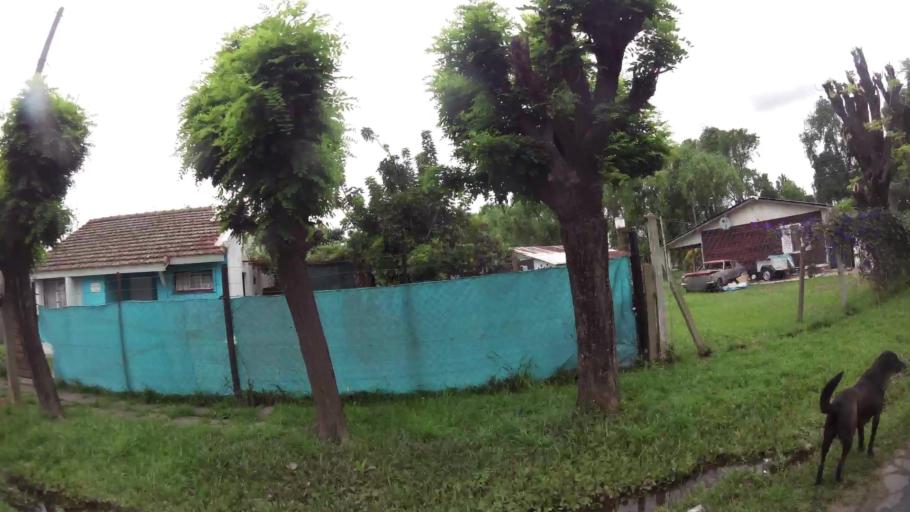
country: AR
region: Buenos Aires
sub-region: Partido de Zarate
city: Zarate
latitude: -34.1164
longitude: -59.0153
